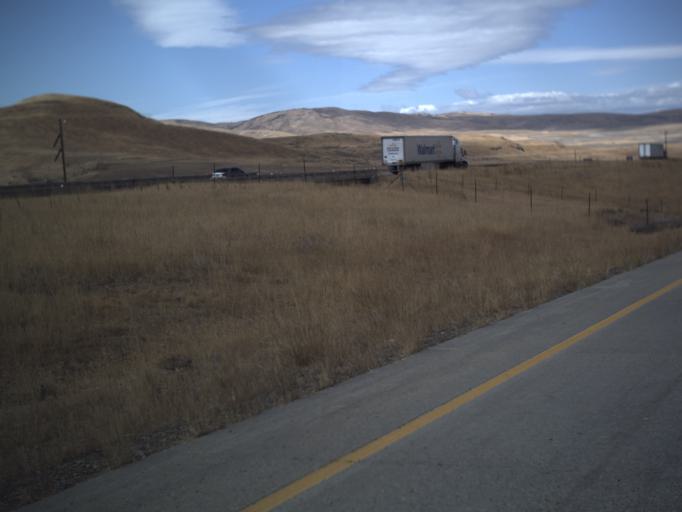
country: US
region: Utah
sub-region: Box Elder County
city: Garland
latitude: 41.8171
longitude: -112.4109
